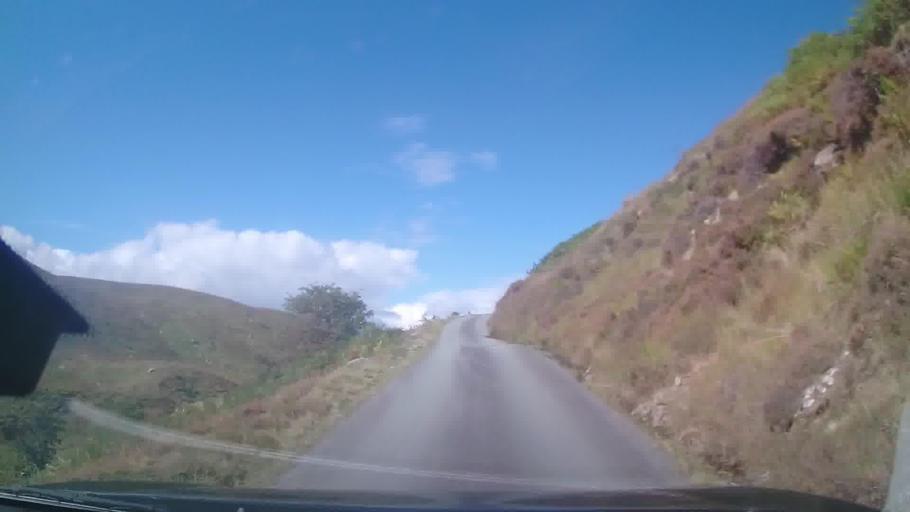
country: GB
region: Wales
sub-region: Gwynedd
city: Bala
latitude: 52.7953
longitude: -3.5660
